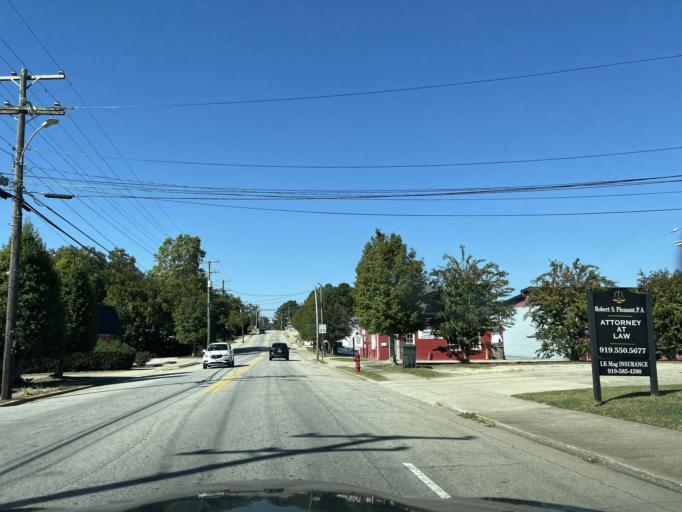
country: US
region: North Carolina
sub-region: Johnston County
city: Clayton
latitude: 35.6543
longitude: -78.4612
